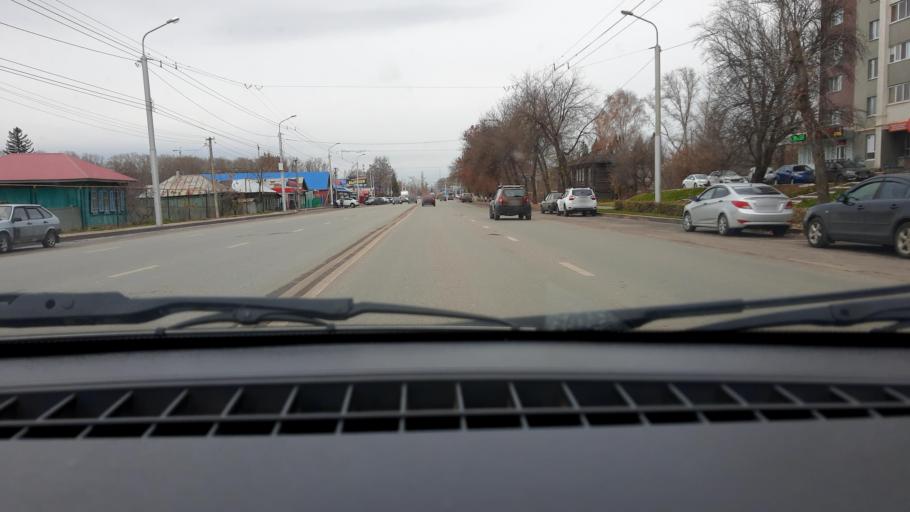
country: RU
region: Bashkortostan
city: Mikhaylovka
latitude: 54.7812
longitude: 55.8884
